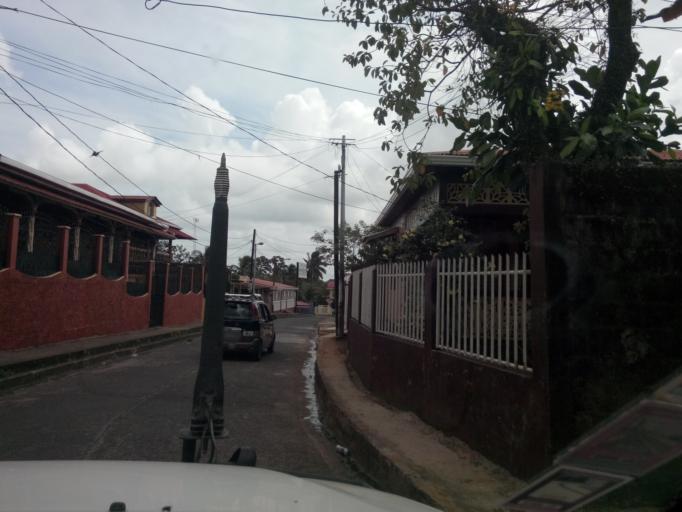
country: NI
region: Atlantico Sur
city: Bluefields
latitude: 12.0151
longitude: -83.7614
